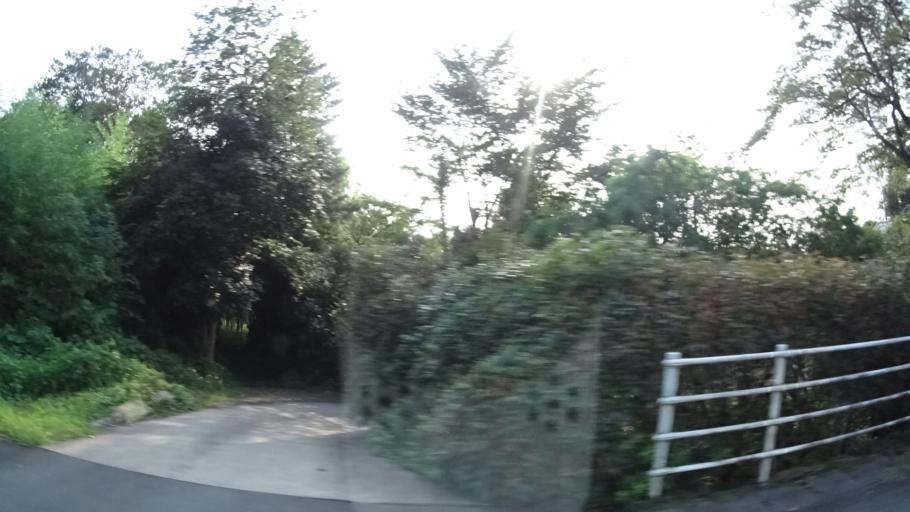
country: JP
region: Tochigi
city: Motegi
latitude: 36.5620
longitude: 140.1032
